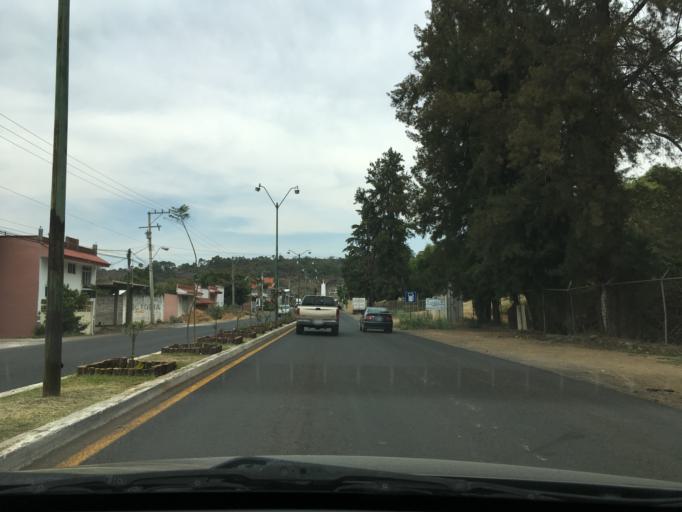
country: MX
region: Michoacan
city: Nuevo San Juan Parangaricutiro
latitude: 19.4097
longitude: -102.1153
